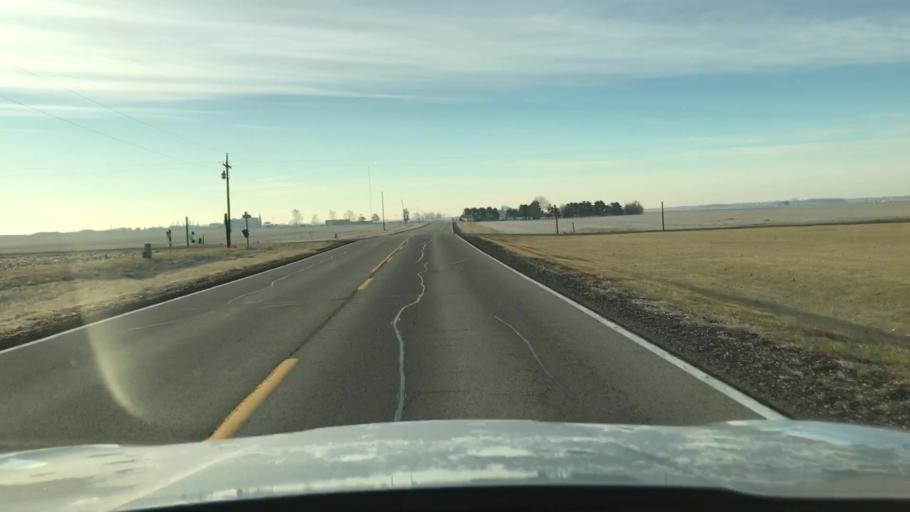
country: US
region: Illinois
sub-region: McLean County
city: Hudson
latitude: 40.5917
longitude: -88.9448
